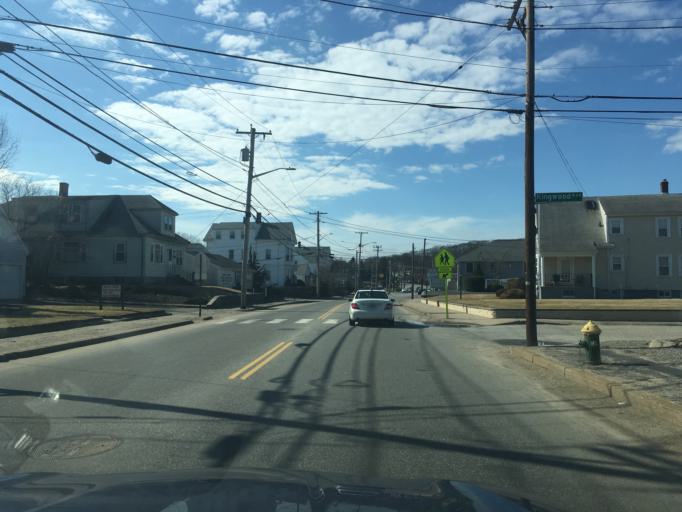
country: US
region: Rhode Island
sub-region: Providence County
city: Cranston
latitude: 41.7813
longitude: -71.4699
